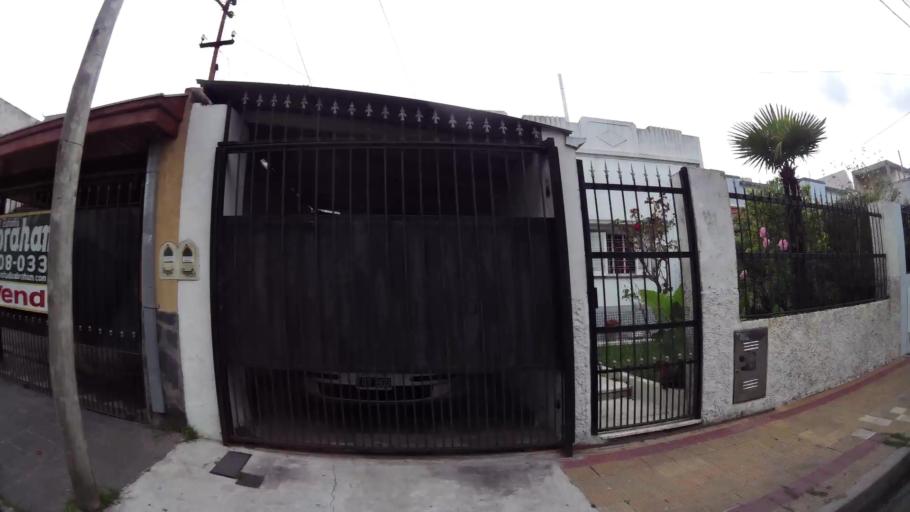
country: AR
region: Buenos Aires
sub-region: Partido de Lanus
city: Lanus
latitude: -34.6814
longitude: -58.3930
